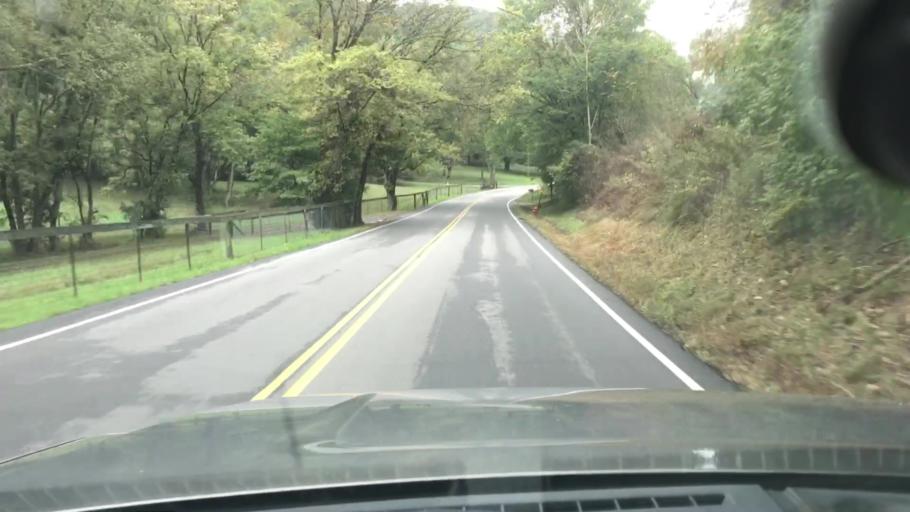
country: US
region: Tennessee
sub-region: Williamson County
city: Brentwood Estates
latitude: 35.9893
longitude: -86.8290
